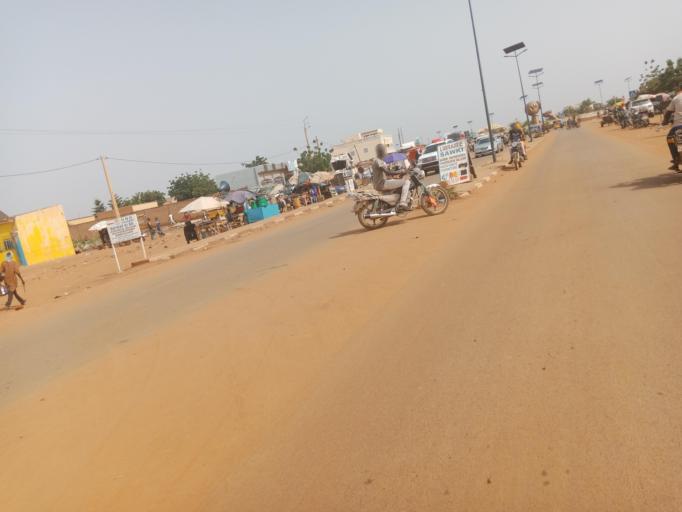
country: NE
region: Tahoua
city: Tahoua
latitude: 14.8827
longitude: 5.2841
